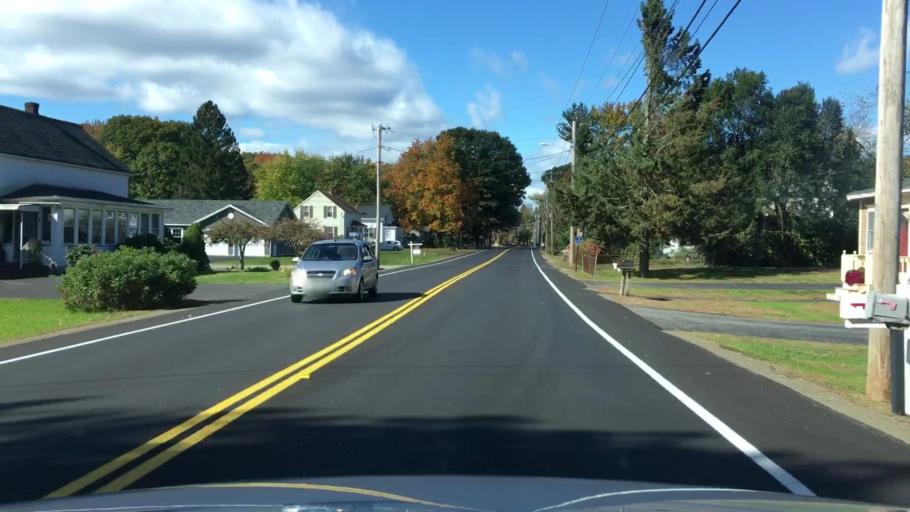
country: US
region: Maine
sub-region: York County
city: Biddeford
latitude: 43.4672
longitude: -70.4454
